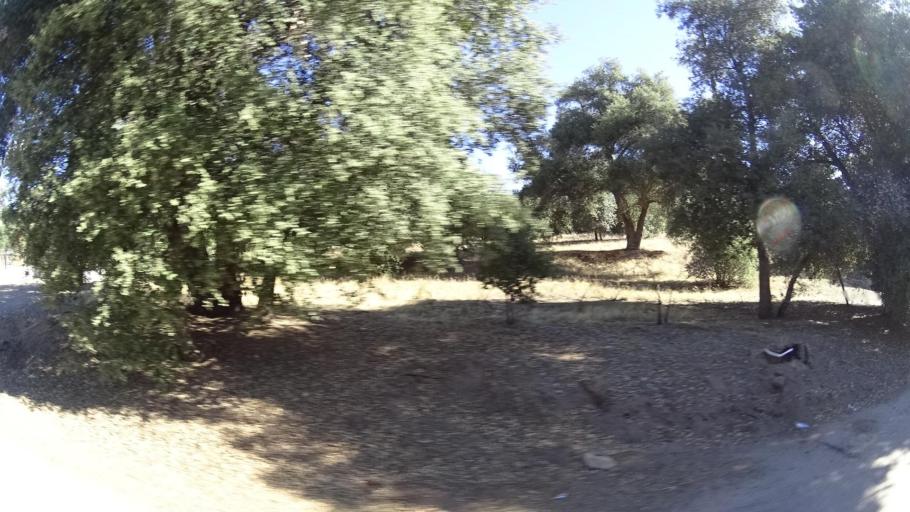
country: US
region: California
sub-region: San Diego County
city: Pine Valley
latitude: 32.8518
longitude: -116.5644
